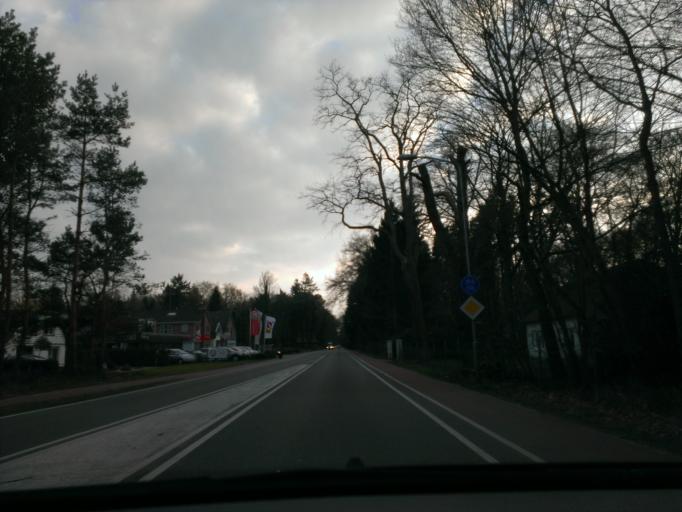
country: NL
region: Gelderland
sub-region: Gemeente Heerde
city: Heerde
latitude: 52.4274
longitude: 6.0645
